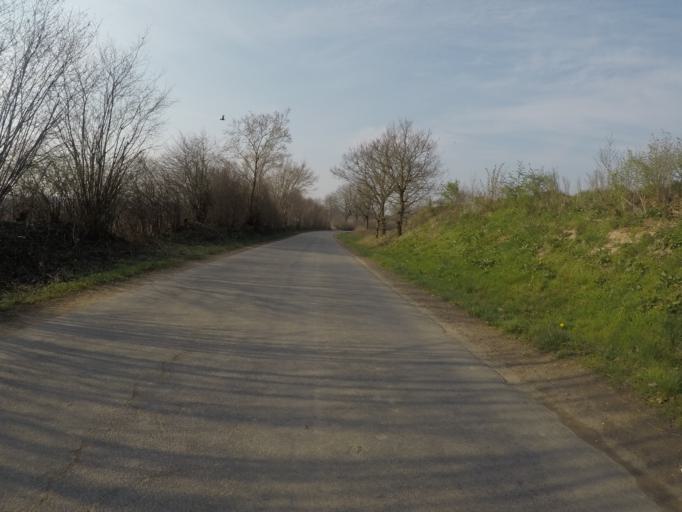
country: DE
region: Schleswig-Holstein
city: Leezen
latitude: 53.8746
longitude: 10.2397
